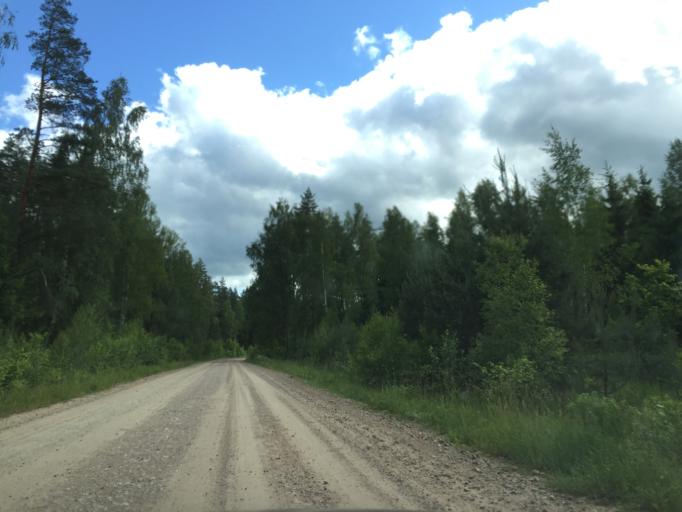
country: LV
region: Vecumnieki
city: Vecumnieki
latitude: 56.4937
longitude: 24.4085
